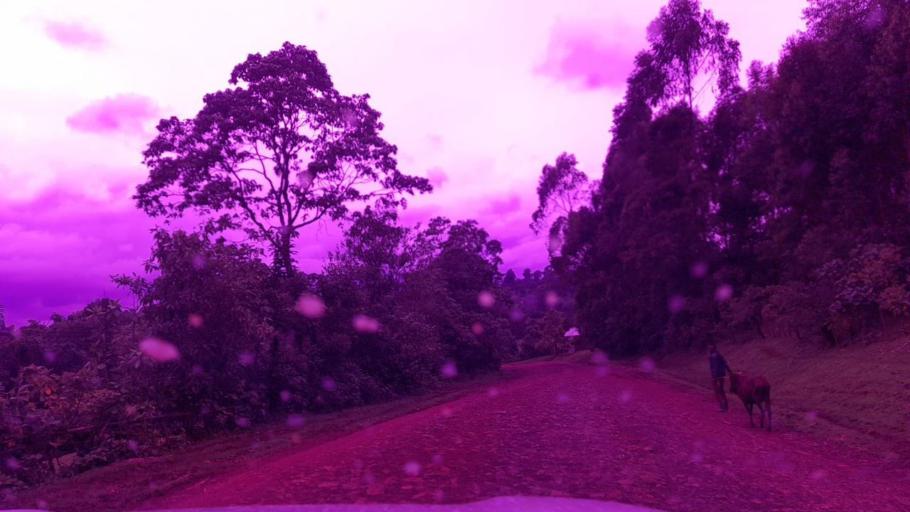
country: ET
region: Southern Nations, Nationalities, and People's Region
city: Tippi
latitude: 7.5785
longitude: 35.6650
